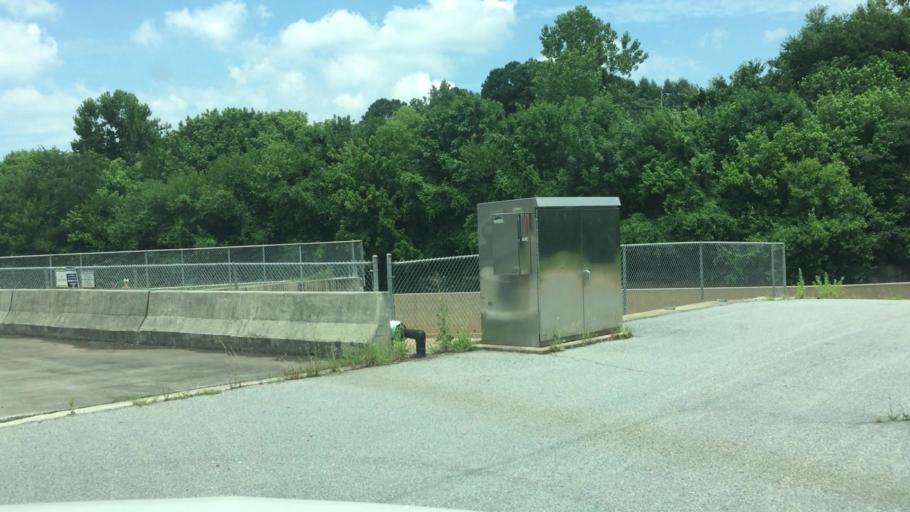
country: US
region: Georgia
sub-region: Fulton County
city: Atlanta
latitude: 33.7185
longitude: -84.3596
